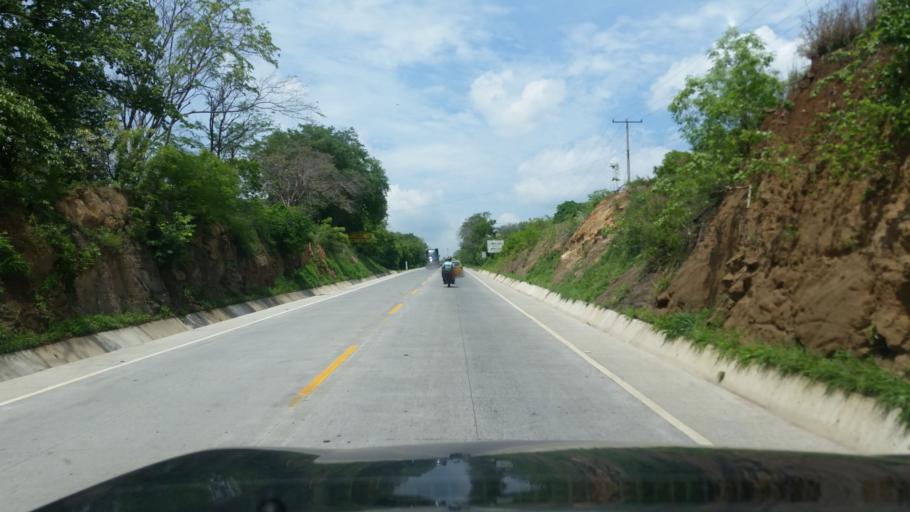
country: NI
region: Managua
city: Carlos Fonseca Amador
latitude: 12.0627
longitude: -86.4640
